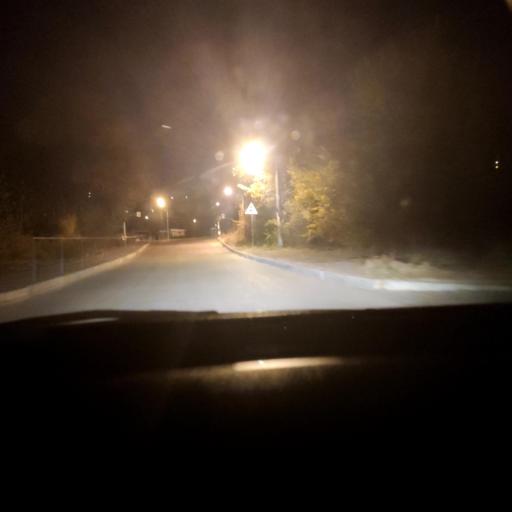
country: RU
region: Voronezj
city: Podgornoye
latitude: 51.7068
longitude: 39.1361
